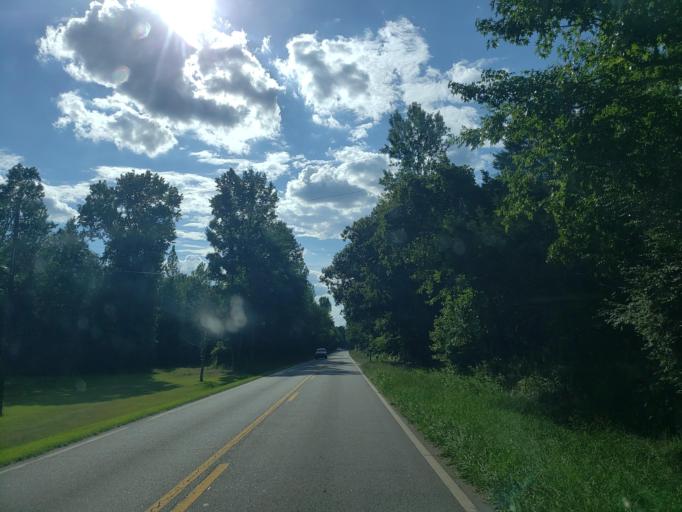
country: US
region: Georgia
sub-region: Bartow County
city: Euharlee
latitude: 34.1812
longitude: -85.0363
